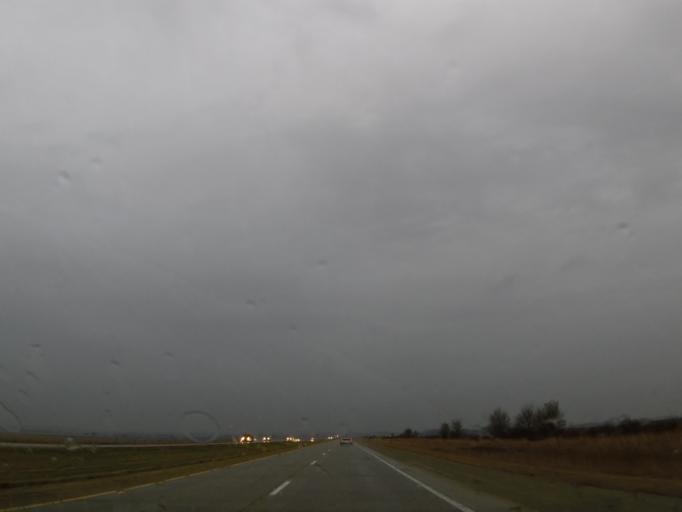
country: US
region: Iowa
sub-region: Floyd County
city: Nora Springs
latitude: 43.1192
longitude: -93.0731
